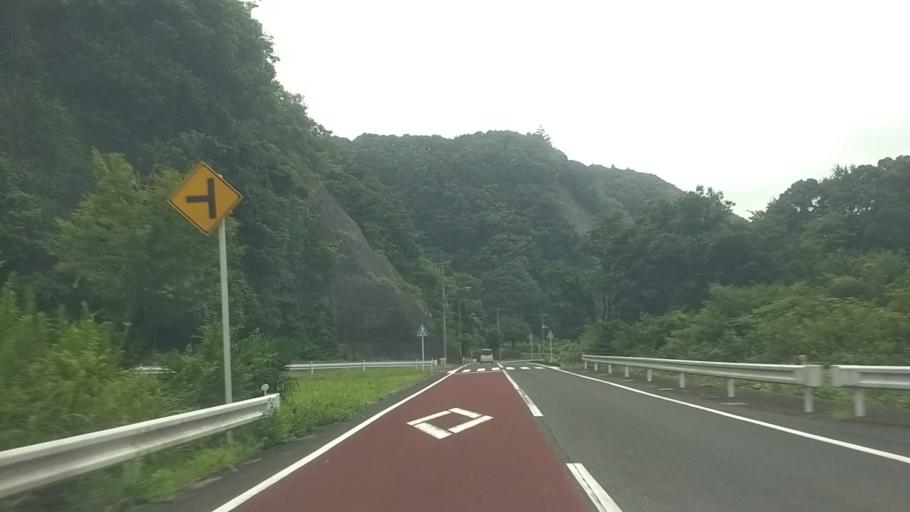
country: JP
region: Chiba
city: Kawaguchi
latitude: 35.2340
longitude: 140.1609
